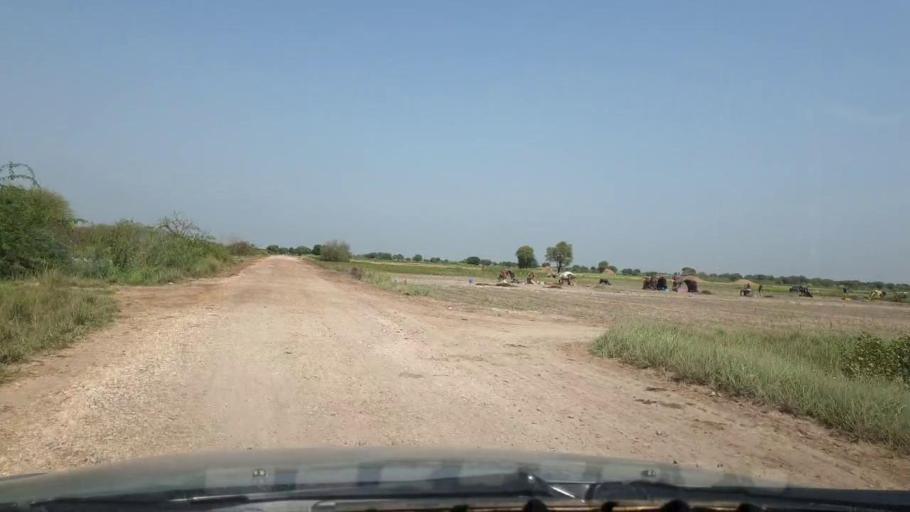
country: PK
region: Sindh
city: Tando Muhammad Khan
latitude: 25.1692
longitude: 68.6338
